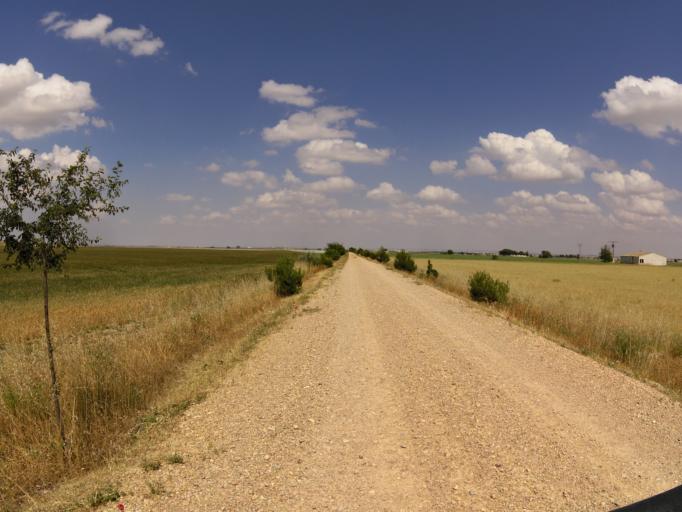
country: ES
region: Castille-La Mancha
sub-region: Provincia de Albacete
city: Pozuelo
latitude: 38.9101
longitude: -2.0254
